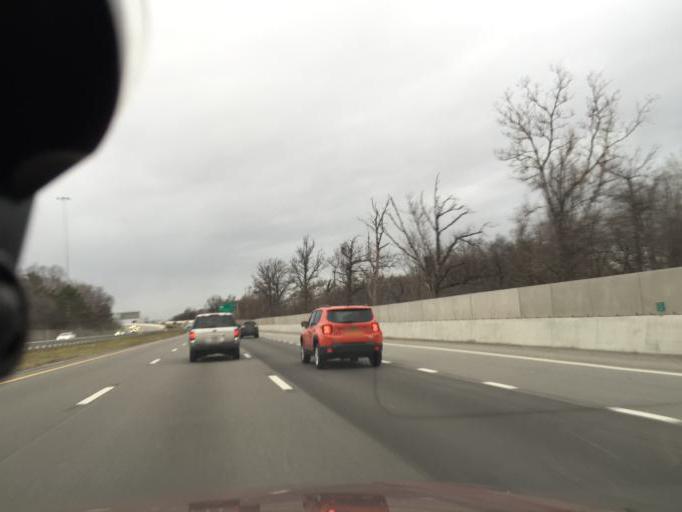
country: US
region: New York
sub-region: Monroe County
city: Rochester
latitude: 43.1181
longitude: -77.6365
